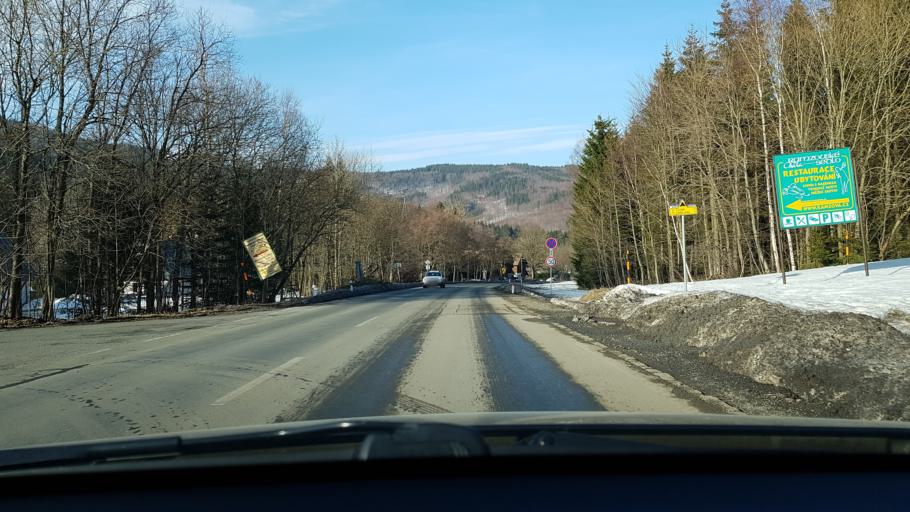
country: CZ
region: Olomoucky
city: Vapenna
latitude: 50.1946
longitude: 17.0647
